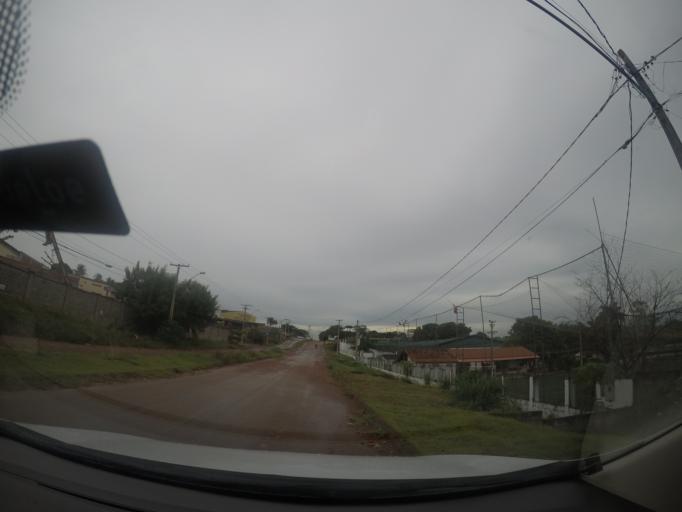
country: BR
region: Goias
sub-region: Goiania
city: Goiania
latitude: -16.6285
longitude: -49.2372
